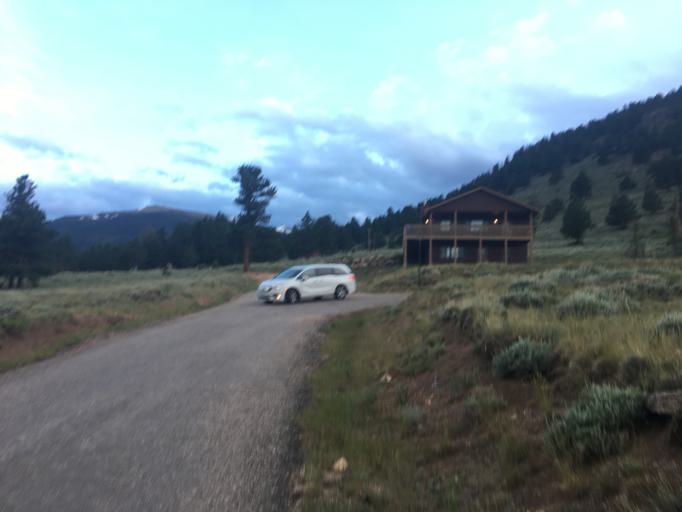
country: US
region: Colorado
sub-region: Larimer County
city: Estes Park
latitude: 40.3338
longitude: -105.5787
